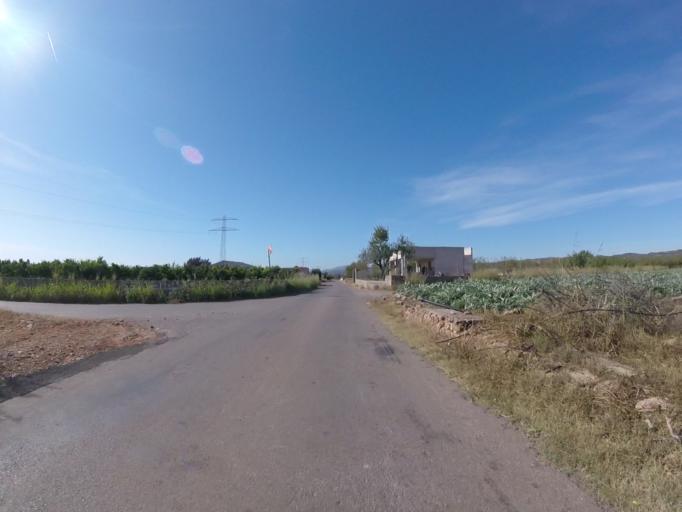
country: ES
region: Valencia
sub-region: Provincia de Castello
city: Torreblanca
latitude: 40.2111
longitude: 0.2109
